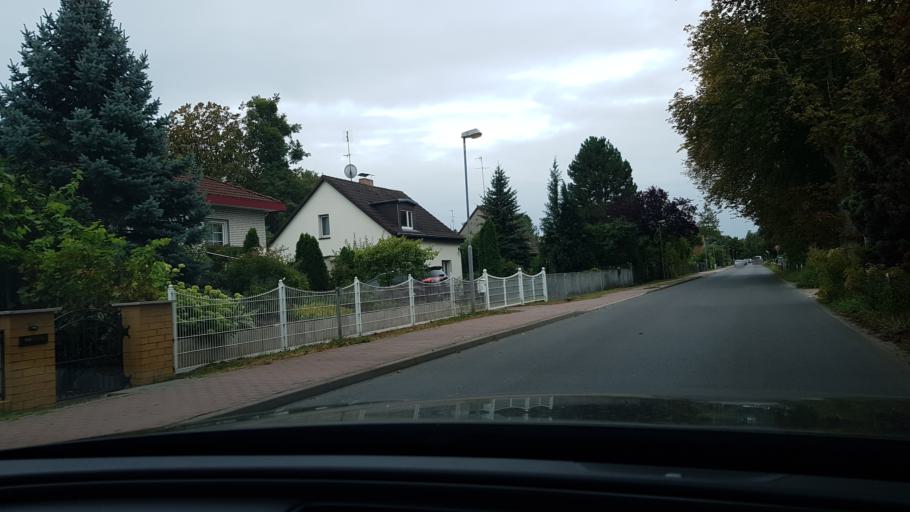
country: DE
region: Brandenburg
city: Brieselang
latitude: 52.5910
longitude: 12.9837
